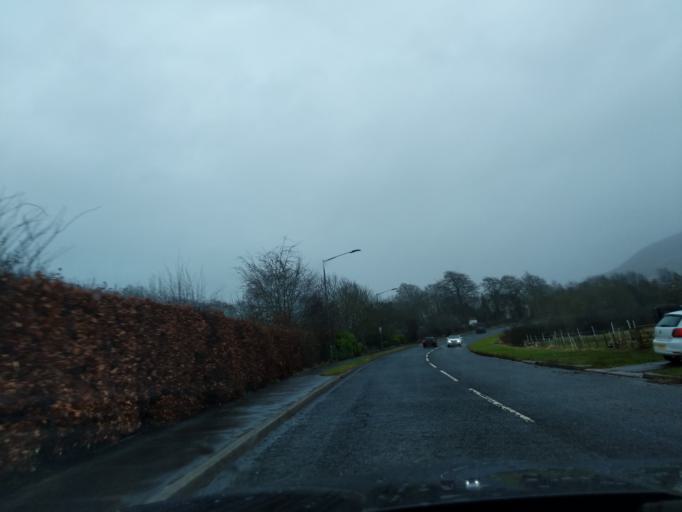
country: GB
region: Scotland
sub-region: The Scottish Borders
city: Melrose
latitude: 55.6021
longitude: -2.7355
